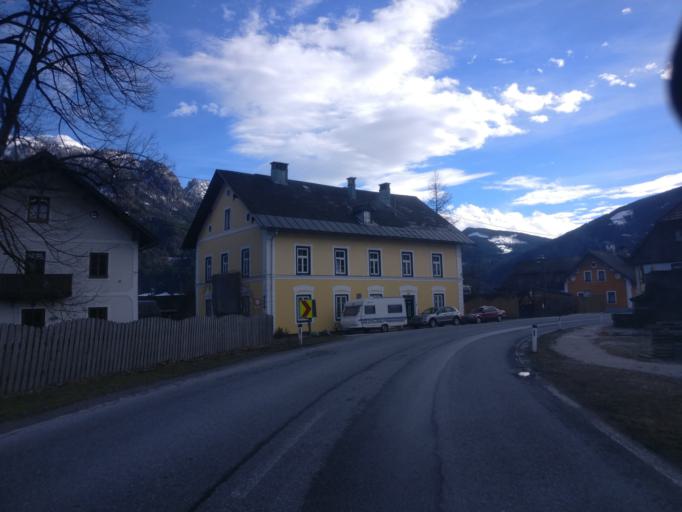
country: AT
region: Styria
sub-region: Politischer Bezirk Liezen
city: Hall bei Admont
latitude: 47.5875
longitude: 14.4704
